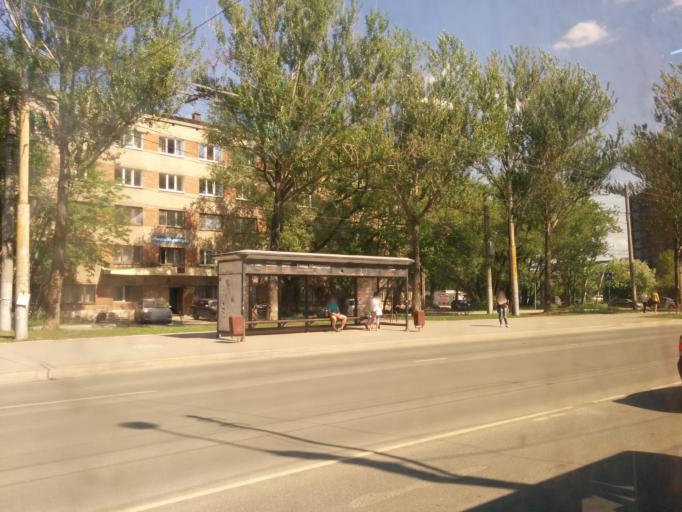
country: RU
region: Perm
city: Perm
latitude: 58.0078
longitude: 56.2833
